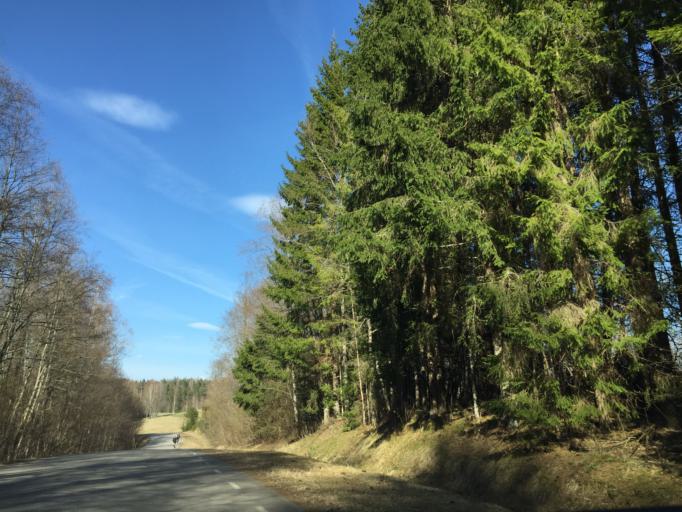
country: EE
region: Vorumaa
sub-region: Antsla vald
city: Vana-Antsla
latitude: 58.0183
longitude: 26.4653
